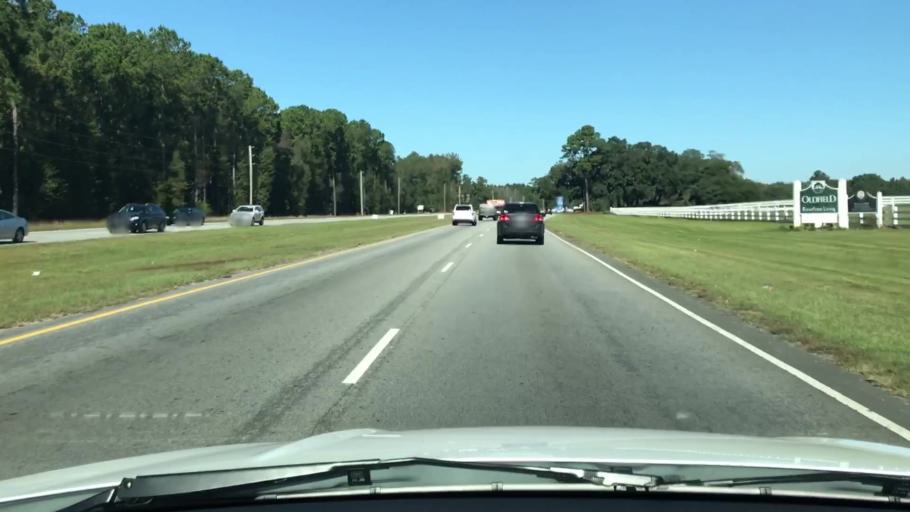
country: US
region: South Carolina
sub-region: Beaufort County
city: Bluffton
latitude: 32.3442
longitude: -80.9274
